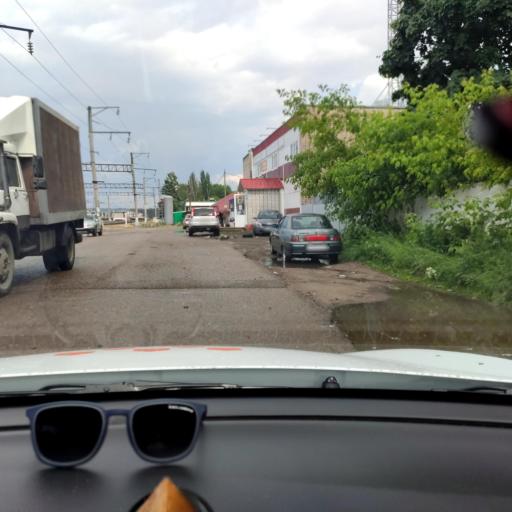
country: RU
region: Tatarstan
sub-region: Zelenodol'skiy Rayon
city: Vasil'yevo
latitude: 55.8370
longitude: 48.7020
